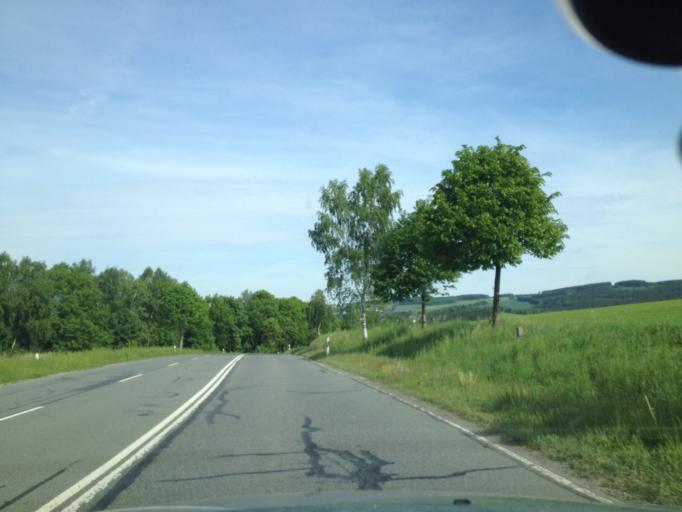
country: DE
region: Saxony
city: Wiesa
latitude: 50.5989
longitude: 13.0009
